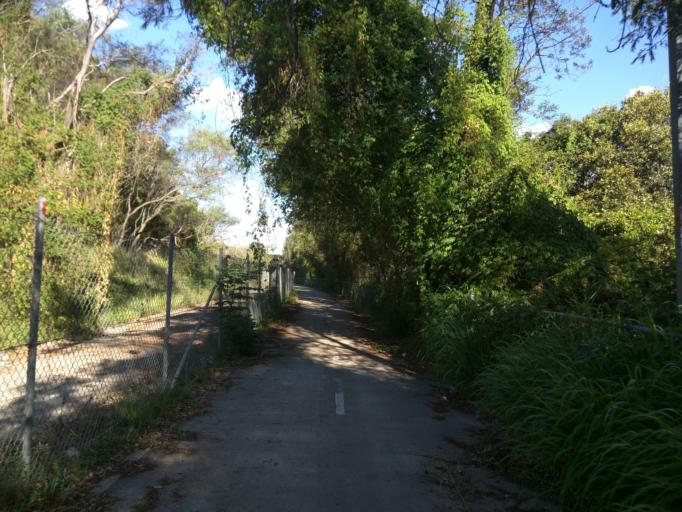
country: AU
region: New South Wales
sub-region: Parramatta
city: Granville
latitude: -33.8347
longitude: 151.0264
